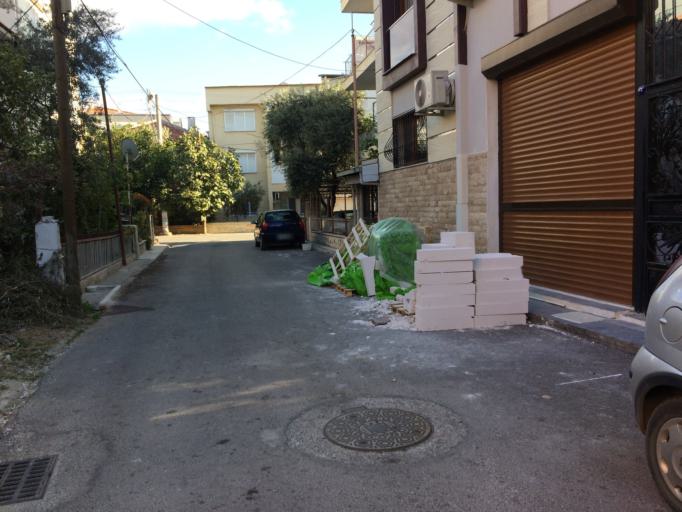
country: TR
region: Izmir
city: Karsiyaka
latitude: 38.4907
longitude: 27.0605
